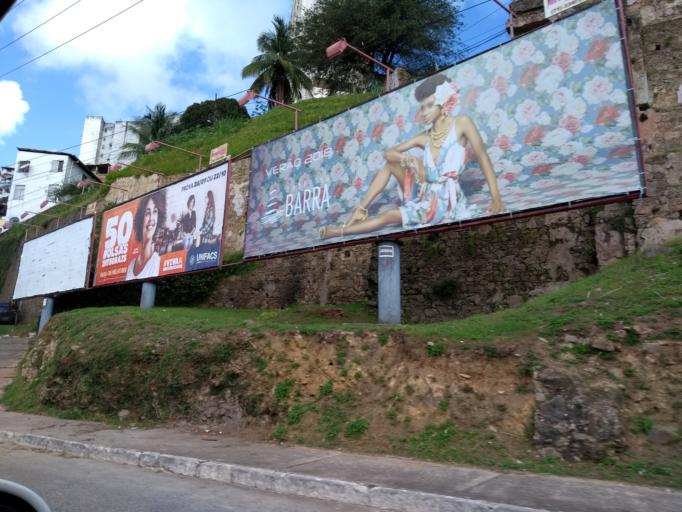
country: BR
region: Bahia
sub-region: Salvador
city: Salvador
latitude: -12.9805
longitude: -38.5187
